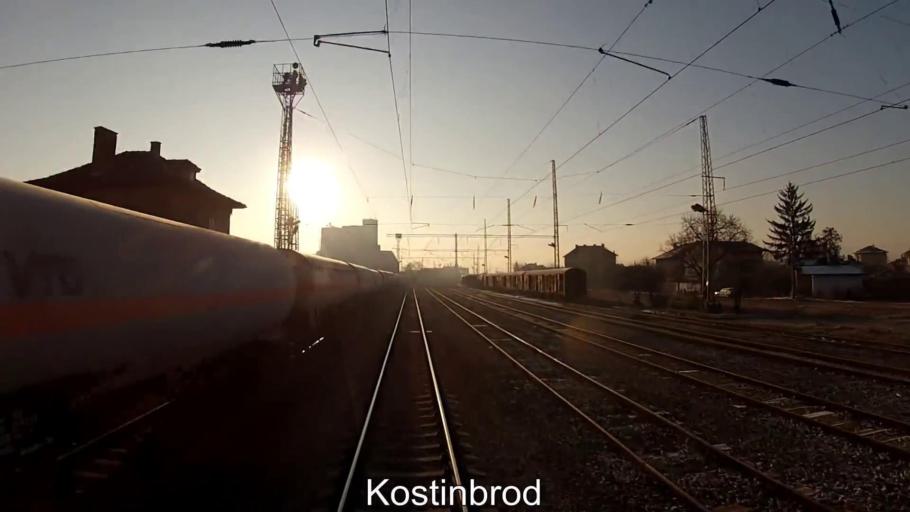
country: BG
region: Sofiya
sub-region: Obshtina Kostinbrod
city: Kostinbrod
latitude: 42.8007
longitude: 23.2041
